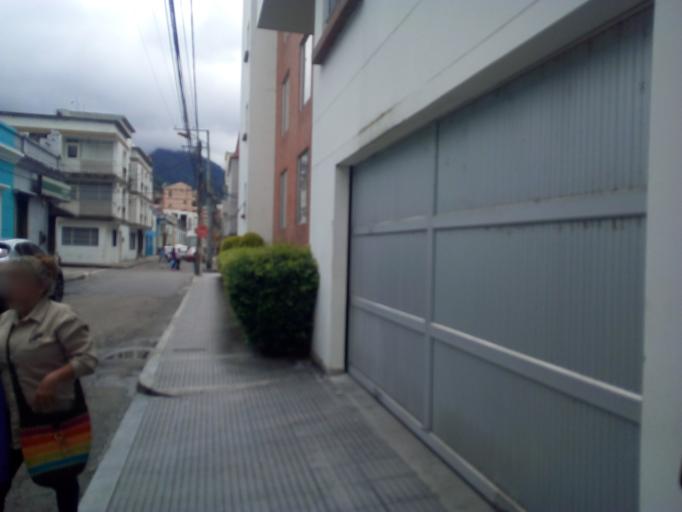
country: CO
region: Tolima
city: Ibague
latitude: 4.4448
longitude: -75.2447
